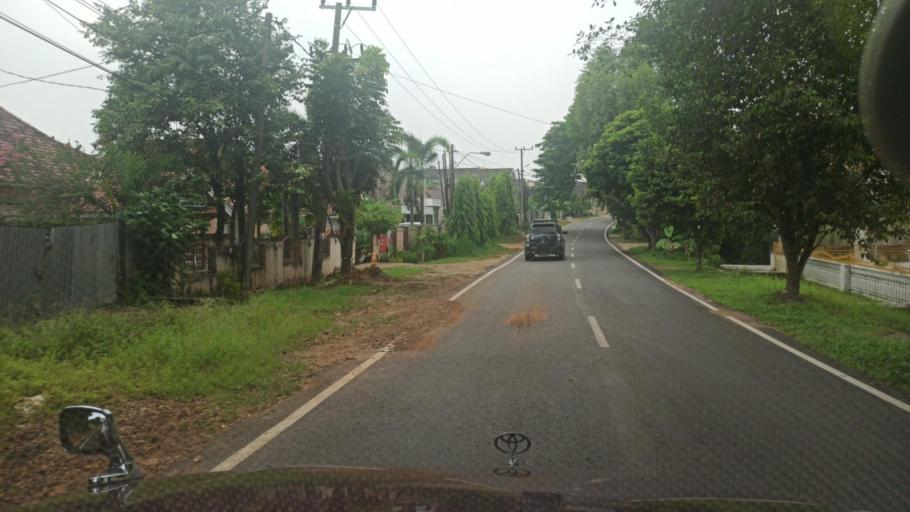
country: ID
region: South Sumatra
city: Plaju
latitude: -2.9950
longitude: 104.7431
